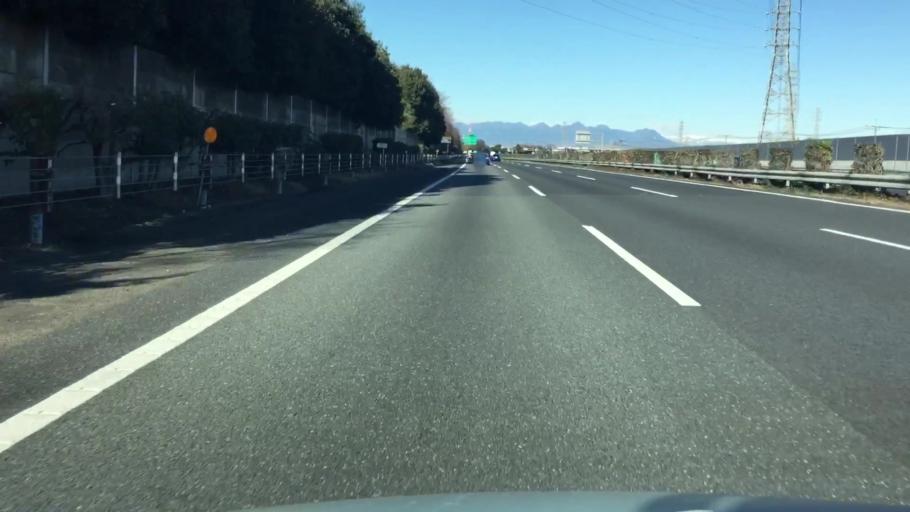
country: JP
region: Saitama
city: Honjo
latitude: 36.2253
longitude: 139.1579
